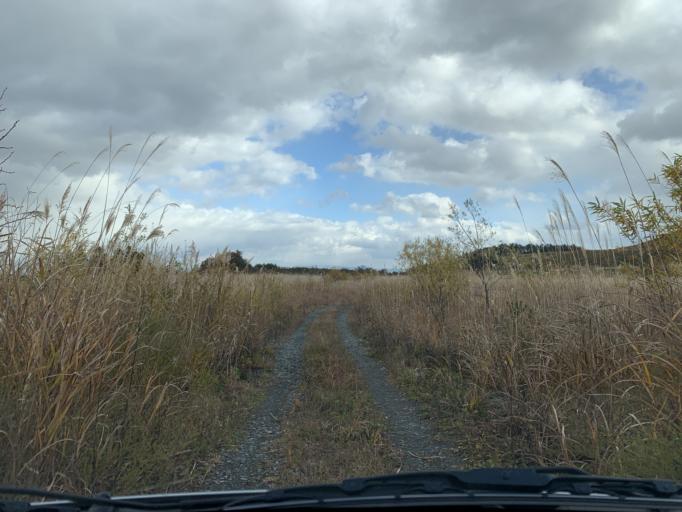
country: JP
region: Iwate
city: Mizusawa
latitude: 39.1130
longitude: 140.9476
